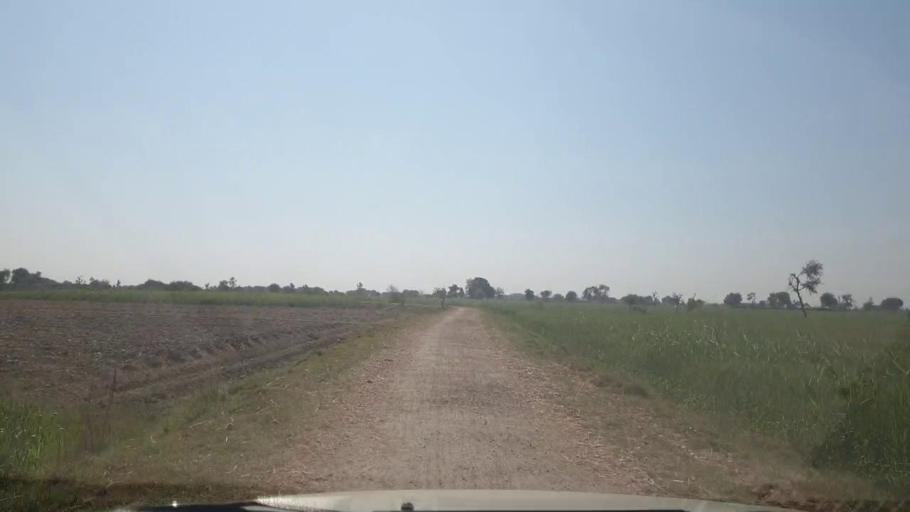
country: PK
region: Sindh
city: Pithoro
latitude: 25.6150
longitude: 69.2030
